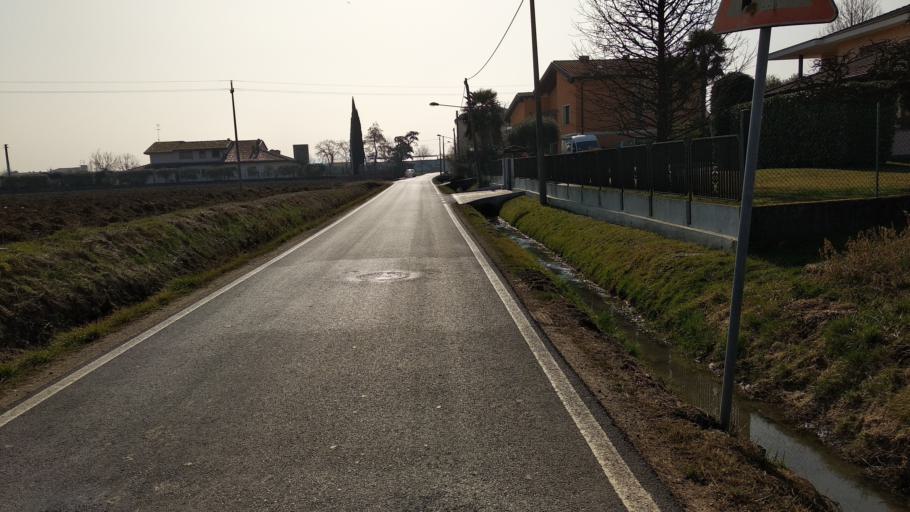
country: IT
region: Veneto
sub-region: Provincia di Vicenza
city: Crispi Cavour
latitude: 45.5858
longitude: 11.5173
